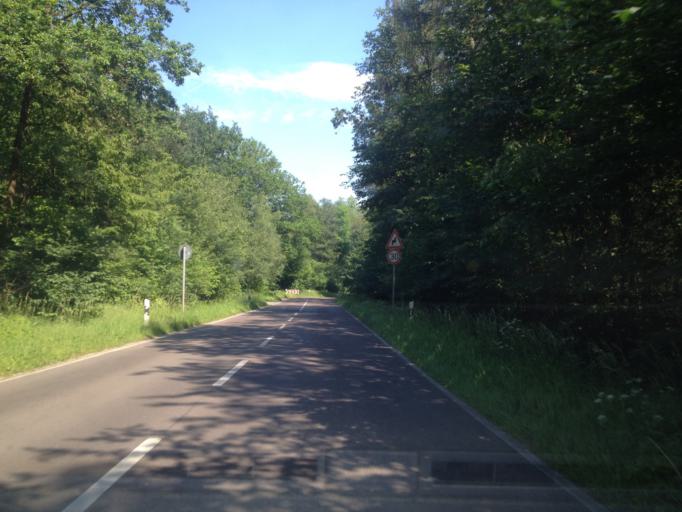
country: DE
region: Berlin
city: Buch
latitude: 52.6451
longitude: 13.4728
